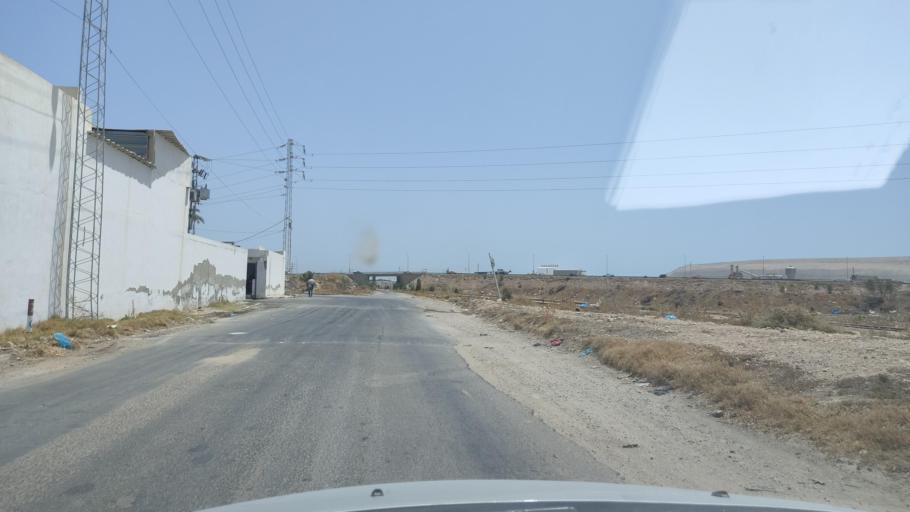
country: TN
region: Safaqis
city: Sfax
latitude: 34.7054
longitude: 10.7171
